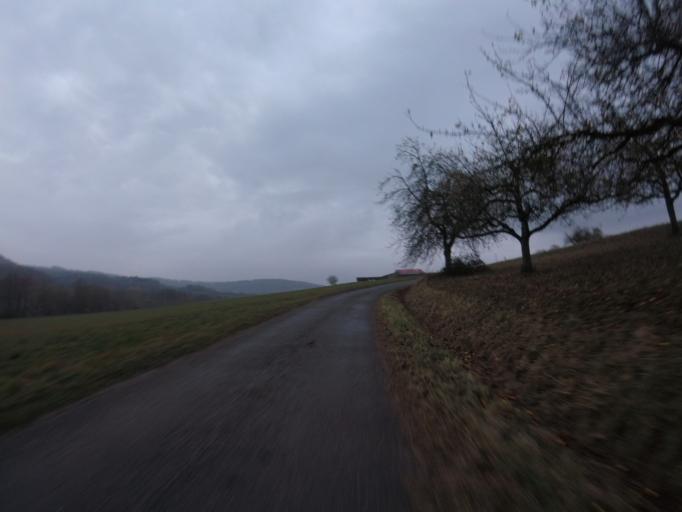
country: DE
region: Baden-Wuerttemberg
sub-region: Regierungsbezirk Stuttgart
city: Aspach
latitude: 48.9986
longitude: 9.3965
